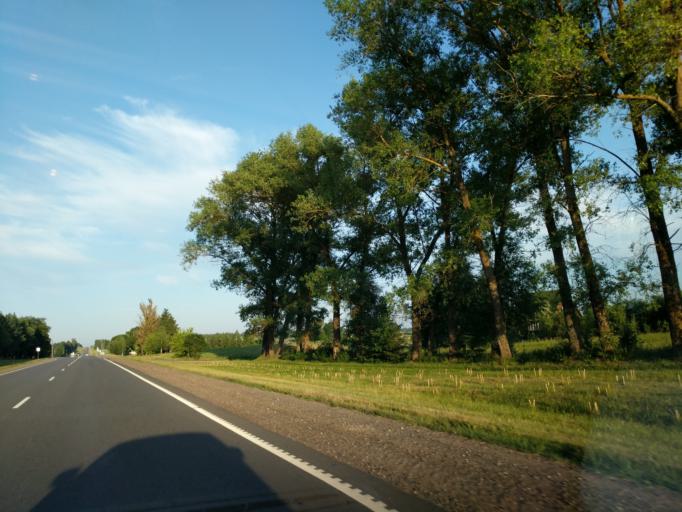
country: BY
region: Minsk
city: Syomkava
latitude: 54.0974
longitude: 27.4970
